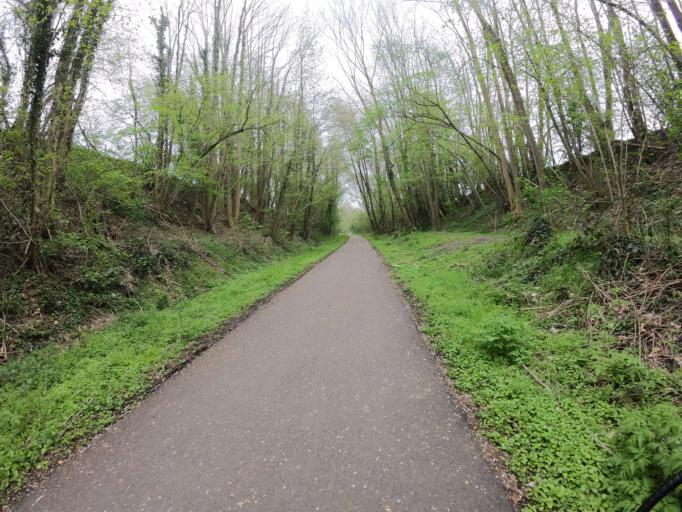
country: BE
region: Wallonia
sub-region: Province du Hainaut
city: Ellezelles
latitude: 50.7450
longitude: 3.6640
